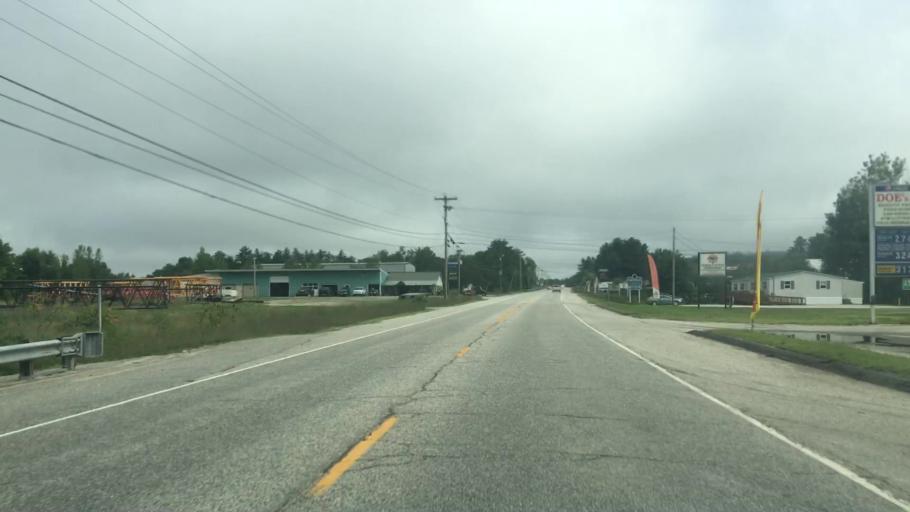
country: US
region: Maine
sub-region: Oxford County
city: South Paris
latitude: 44.2368
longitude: -70.5139
